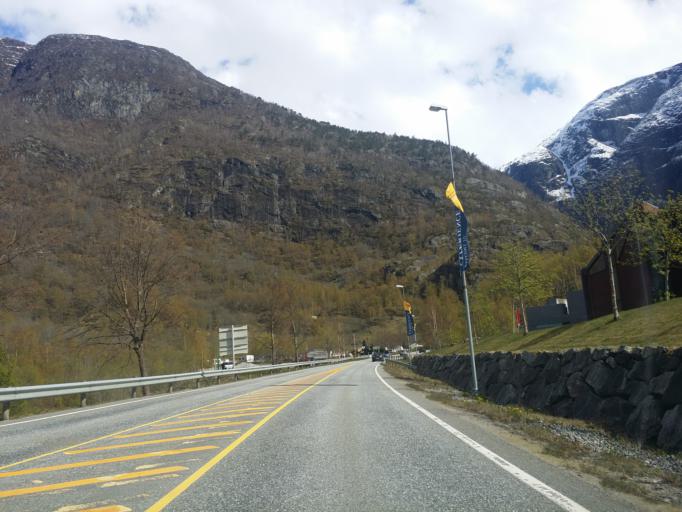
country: NO
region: Hordaland
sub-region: Eidfjord
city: Eidfjord
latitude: 60.4237
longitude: 7.1340
